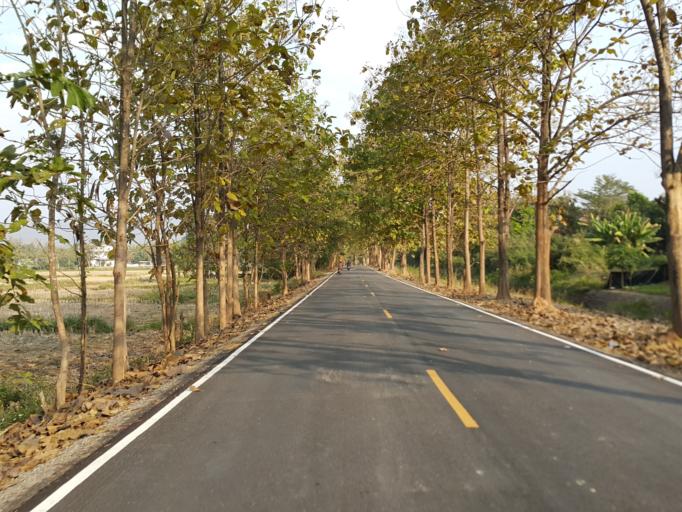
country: TH
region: Chiang Mai
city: San Sai
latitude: 18.8749
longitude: 99.1414
